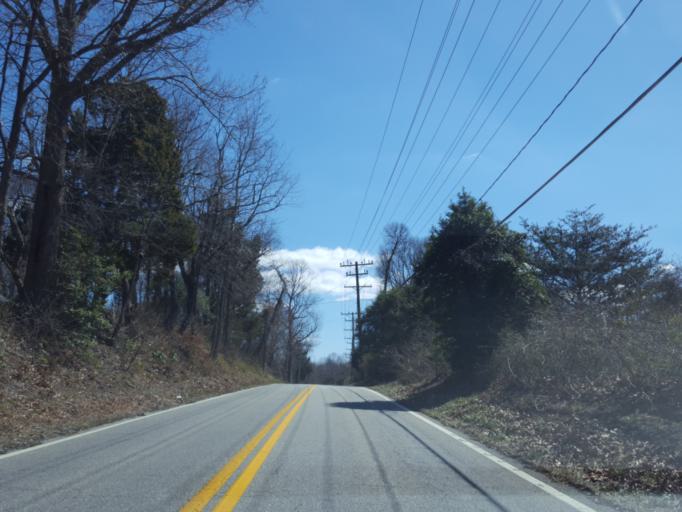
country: US
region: Maryland
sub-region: Calvert County
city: Owings
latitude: 38.7342
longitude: -76.5802
